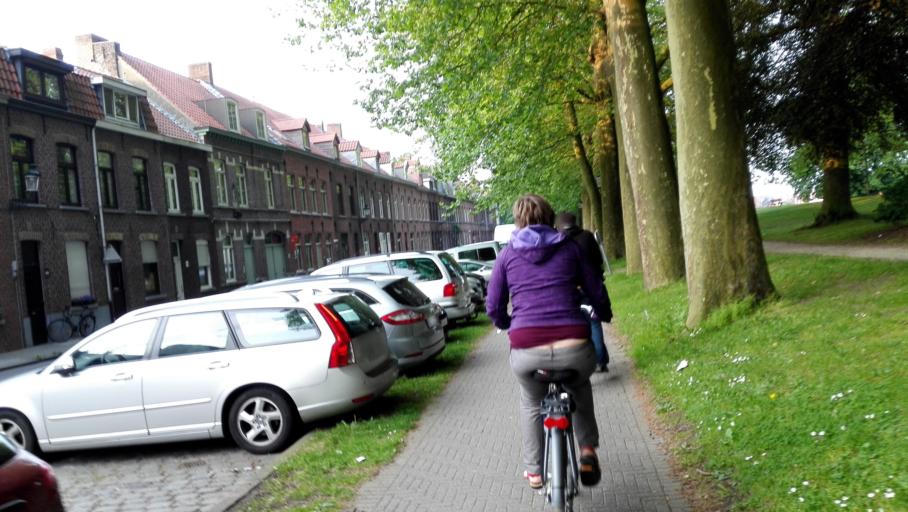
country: BE
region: Flanders
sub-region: Provincie West-Vlaanderen
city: Brugge
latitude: 51.2016
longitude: 3.2320
